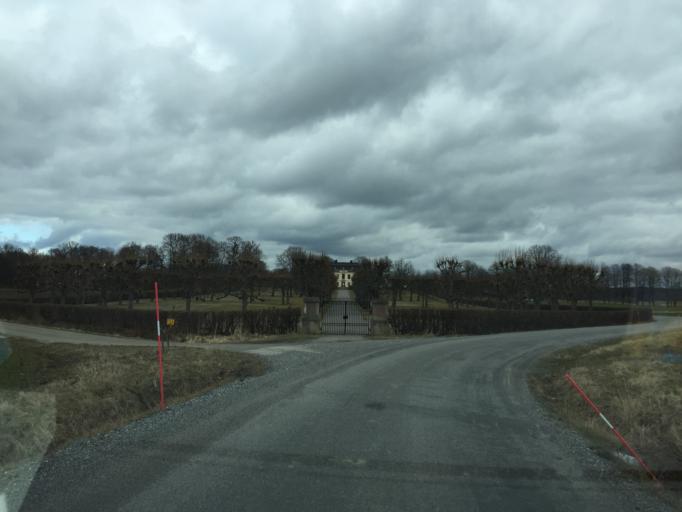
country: SE
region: Stockholm
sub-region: Salems Kommun
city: Ronninge
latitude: 59.2568
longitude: 17.7531
